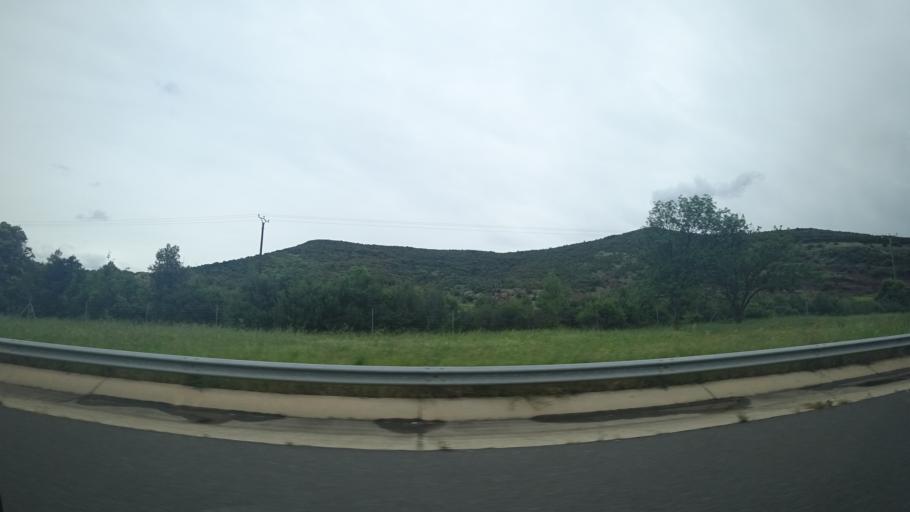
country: FR
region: Languedoc-Roussillon
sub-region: Departement de l'Herault
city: Nebian
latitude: 43.6798
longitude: 3.3958
